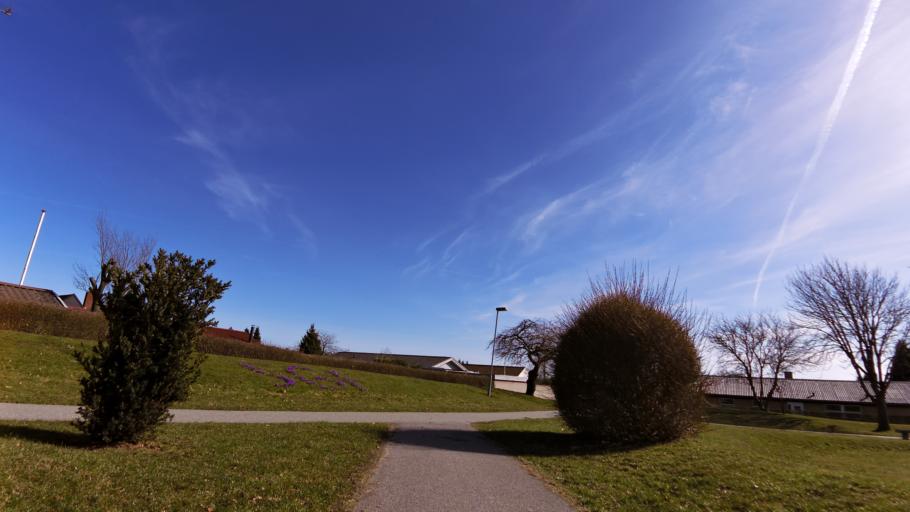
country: DK
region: Central Jutland
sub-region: Arhus Kommune
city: Stavtrup
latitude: 56.1788
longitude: 10.1038
